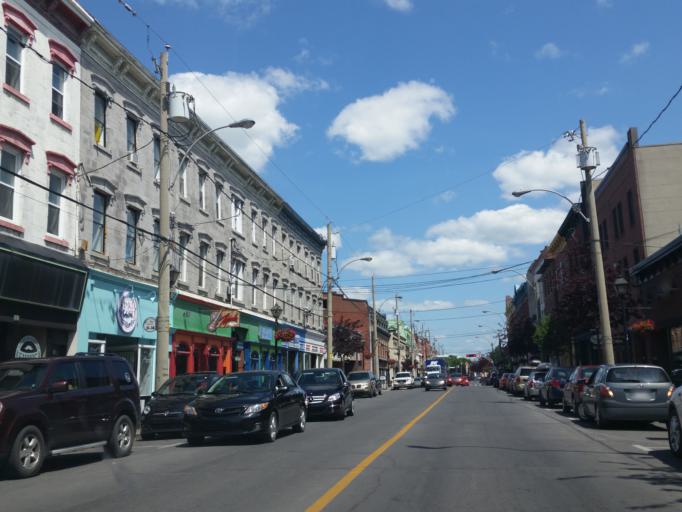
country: CA
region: Quebec
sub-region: Monteregie
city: Saint-Jean-sur-Richelieu
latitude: 45.3048
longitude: -73.2508
